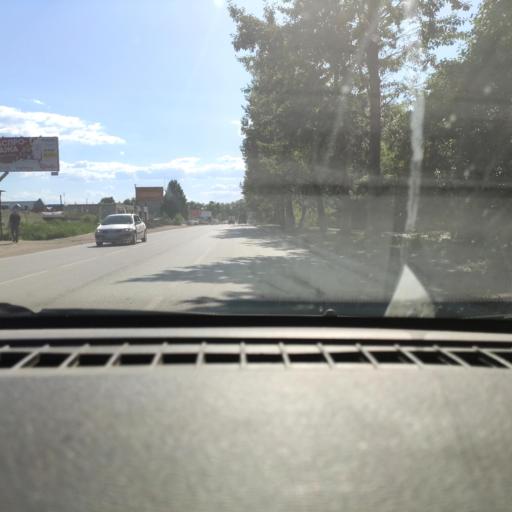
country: RU
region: Perm
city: Krasnokamsk
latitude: 58.0806
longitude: 55.7627
